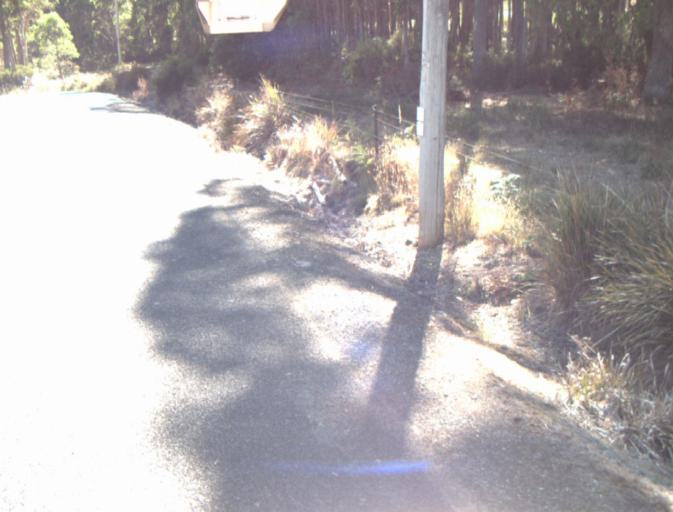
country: AU
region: Tasmania
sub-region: Launceston
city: Newstead
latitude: -41.3119
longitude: 147.3344
